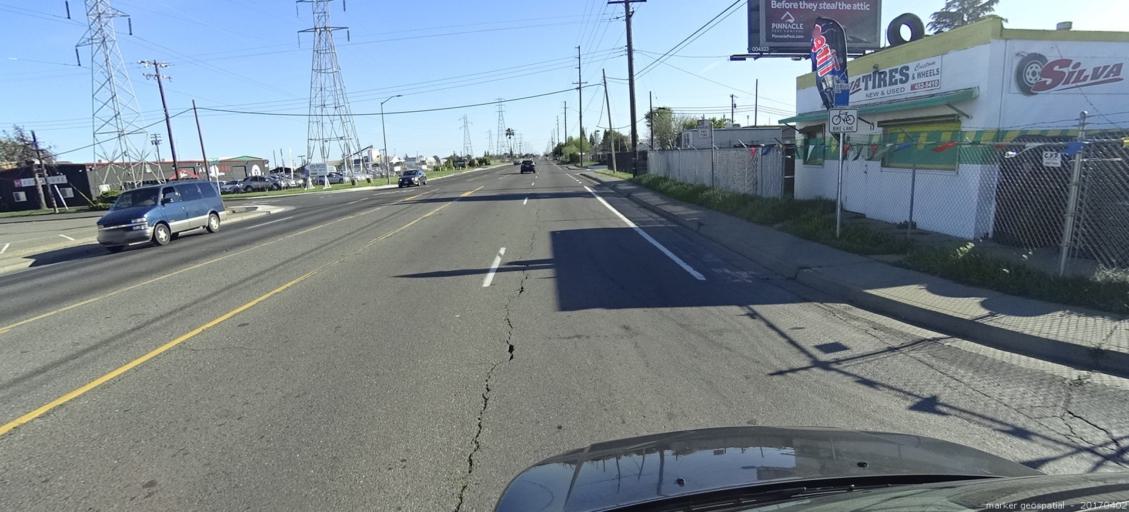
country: US
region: California
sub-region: Sacramento County
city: Florin
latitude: 38.5360
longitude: -121.4093
